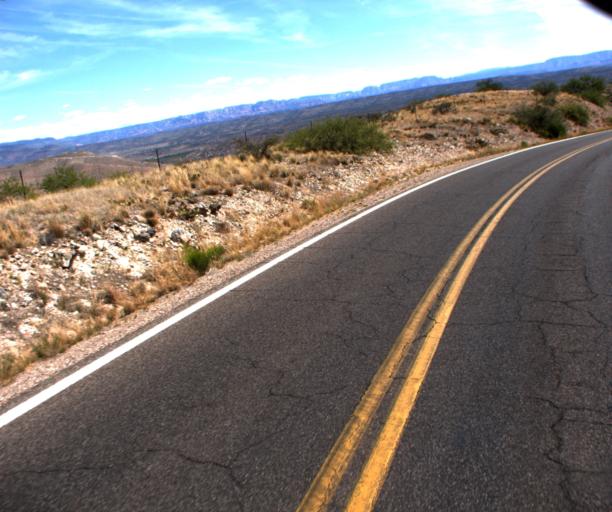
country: US
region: Arizona
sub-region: Yavapai County
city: Clarkdale
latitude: 34.7592
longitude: -112.0830
